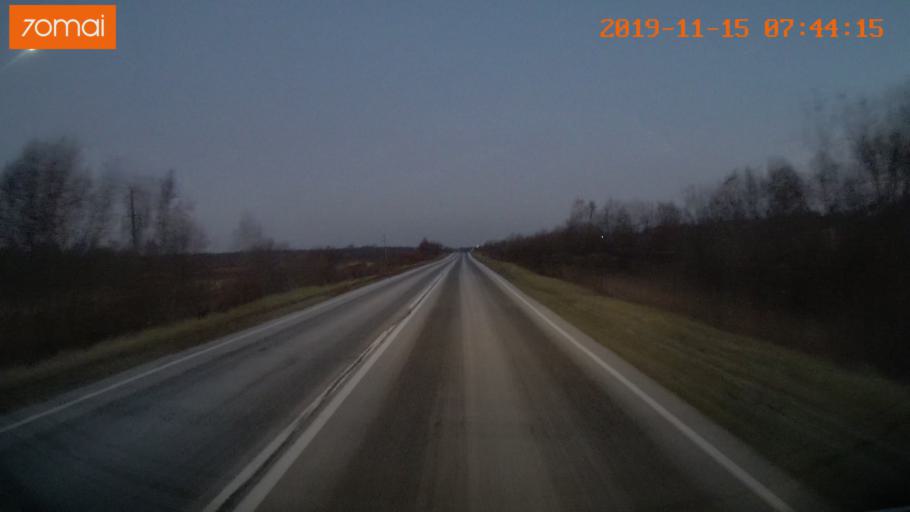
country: RU
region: Vologda
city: Sheksna
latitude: 58.8114
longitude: 38.3158
